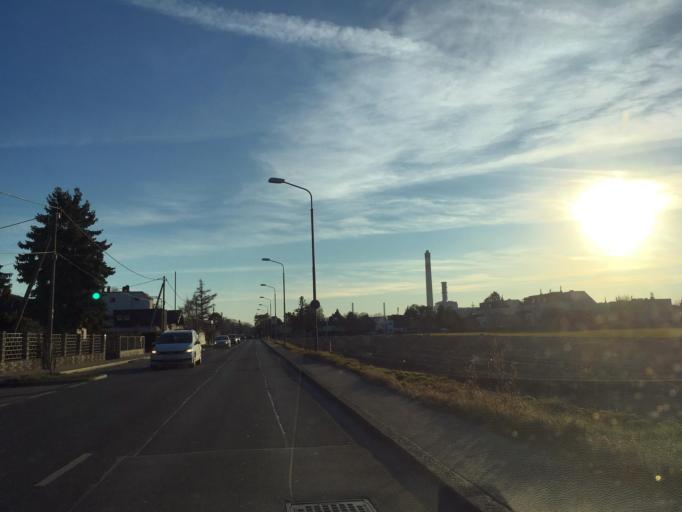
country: AT
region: Lower Austria
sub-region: Politischer Bezirk Wien-Umgebung
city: Schwechat
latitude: 48.2038
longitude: 16.4753
